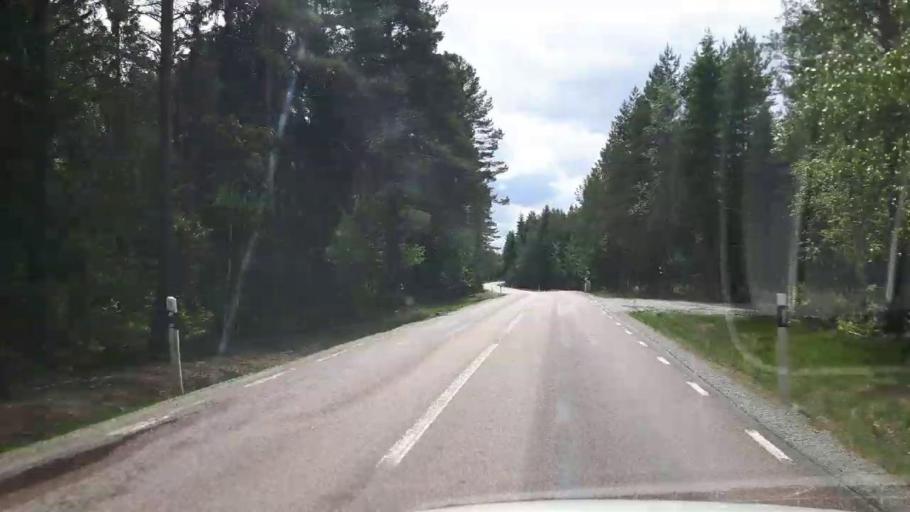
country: SE
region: Vaestmanland
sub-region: Fagersta Kommun
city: Fagersta
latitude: 59.9073
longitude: 15.8234
